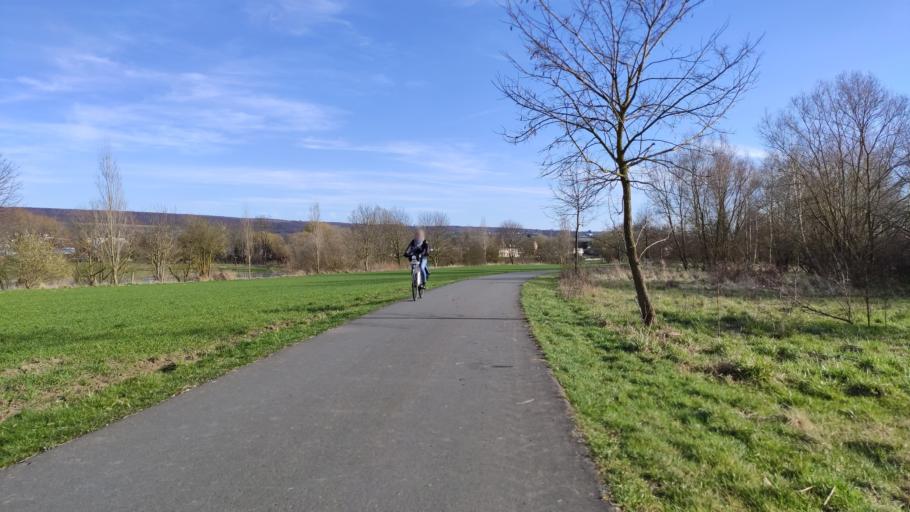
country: DE
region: Lower Saxony
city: Boffzen
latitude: 51.7564
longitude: 9.3831
